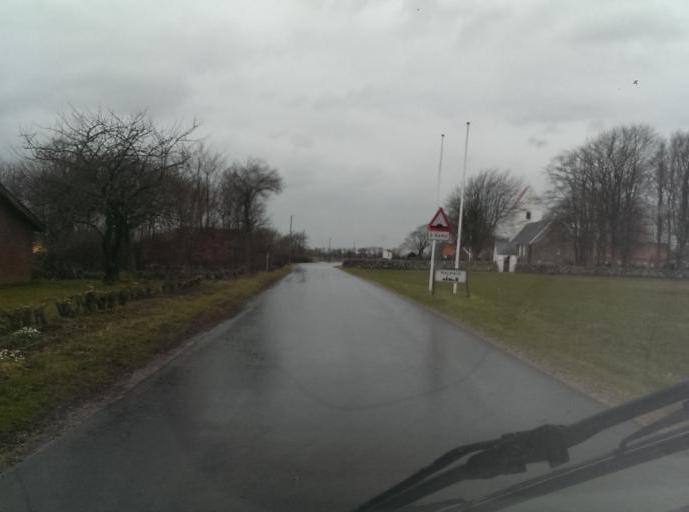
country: DK
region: Central Jutland
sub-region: Ringkobing-Skjern Kommune
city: Skjern
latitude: 56.0513
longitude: 8.4092
